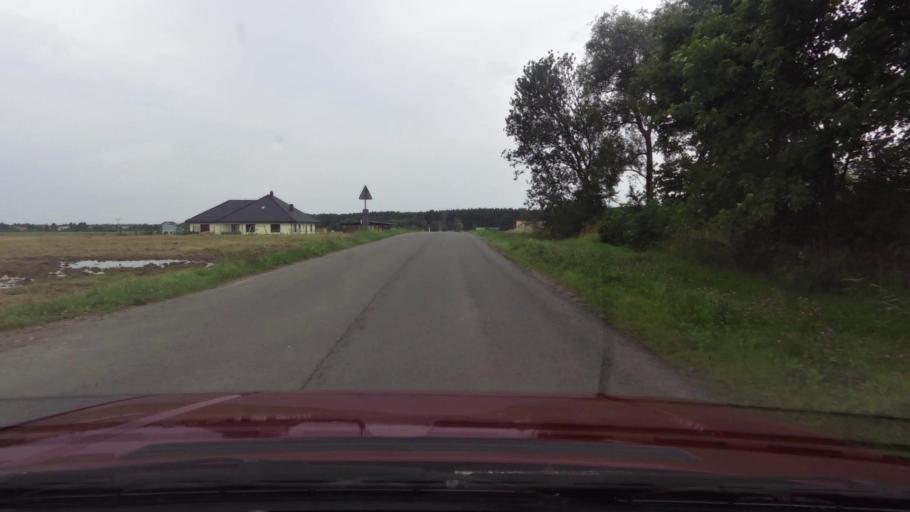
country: PL
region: West Pomeranian Voivodeship
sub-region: Powiat kolobrzeski
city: Grzybowo
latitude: 54.1473
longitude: 15.5092
